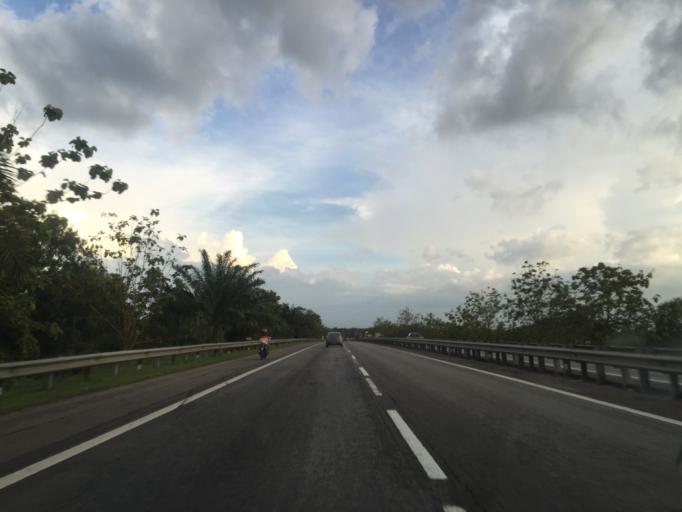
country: MY
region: Kedah
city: Bedong
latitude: 5.7439
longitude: 100.5152
